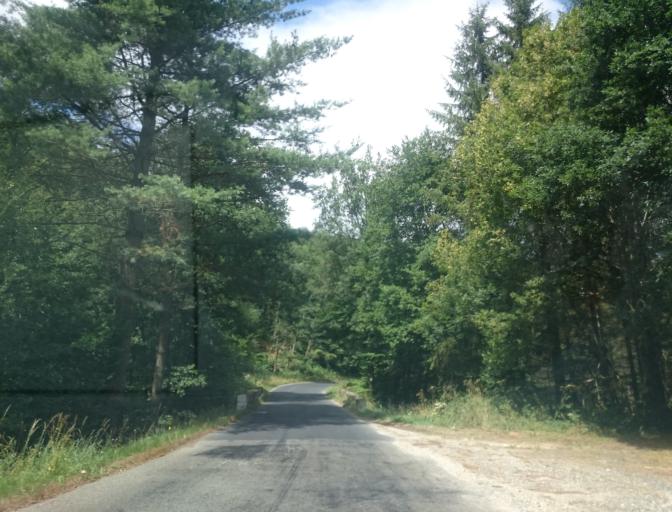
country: FR
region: Auvergne
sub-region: Departement du Cantal
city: Laroquebrou
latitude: 44.9421
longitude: 2.1980
